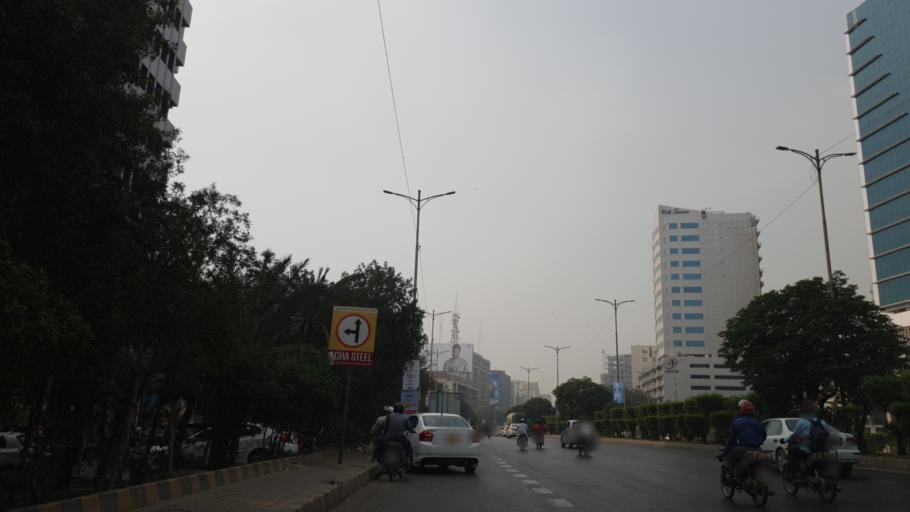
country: PK
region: Sindh
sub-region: Karachi District
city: Karachi
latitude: 24.8642
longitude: 67.0756
